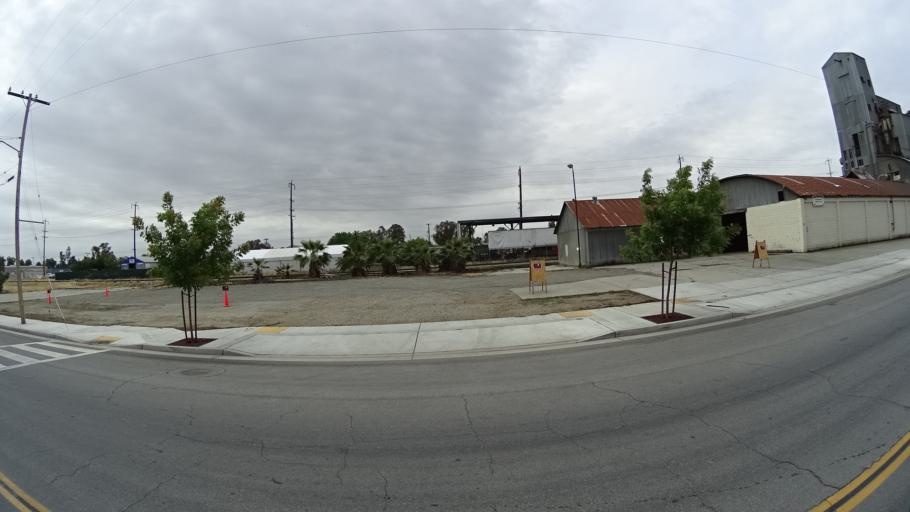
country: US
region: California
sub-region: Kings County
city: Hanford
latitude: 36.3262
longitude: -119.6407
